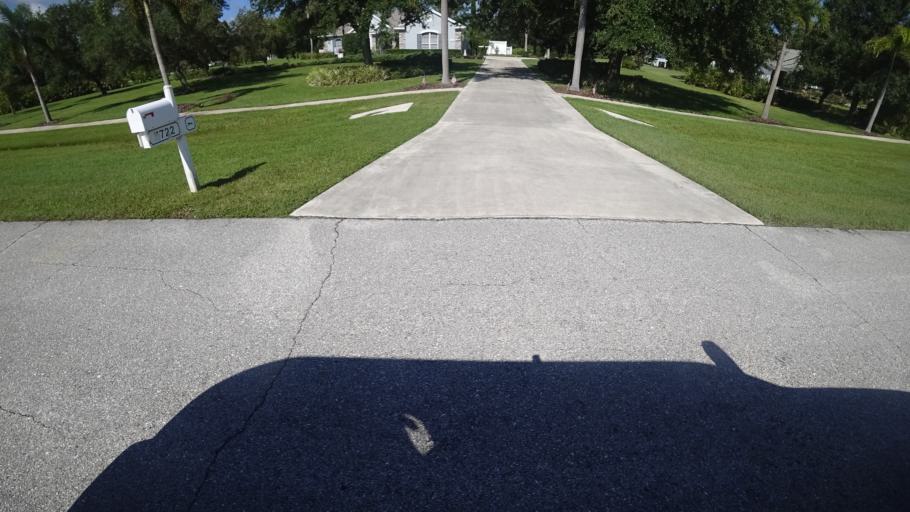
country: US
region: Florida
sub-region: Sarasota County
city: The Meadows
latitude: 27.4024
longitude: -82.3193
